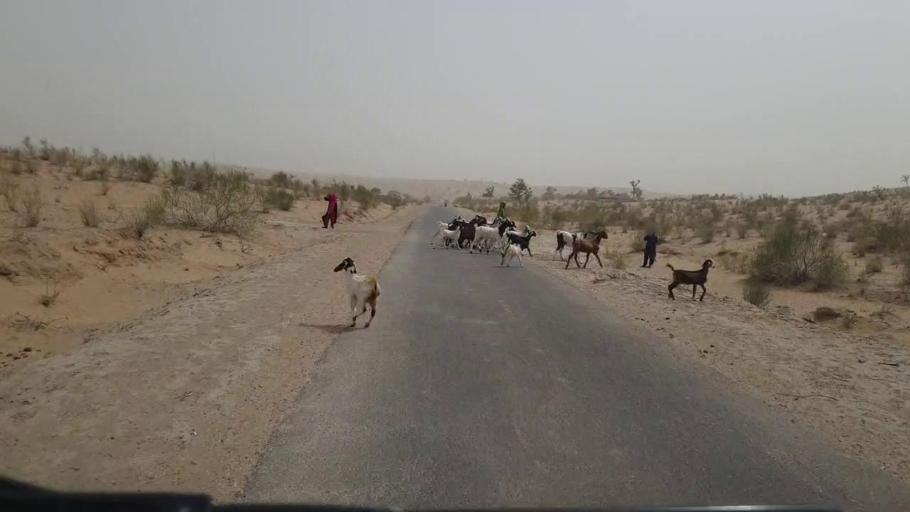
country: PK
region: Sindh
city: Islamkot
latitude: 25.2719
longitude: 70.6525
